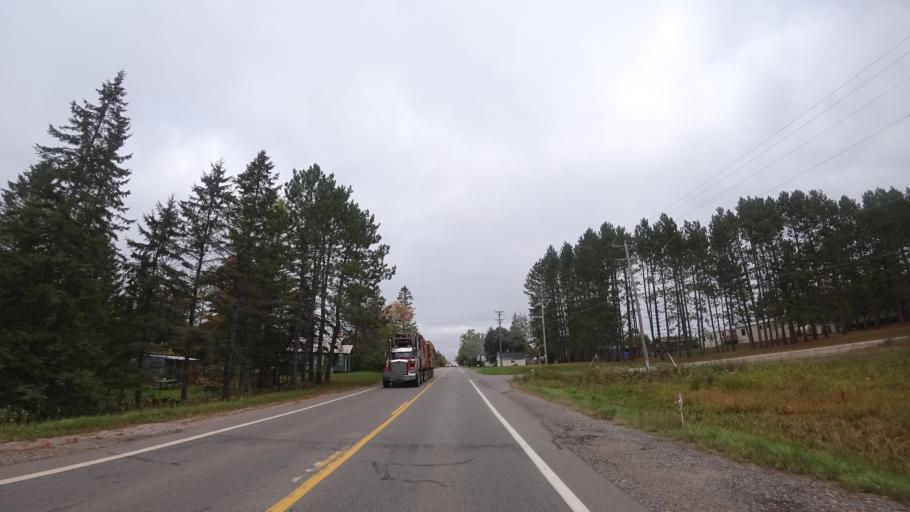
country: US
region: Michigan
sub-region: Iron County
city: Crystal Falls
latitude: 46.1338
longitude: -88.0926
